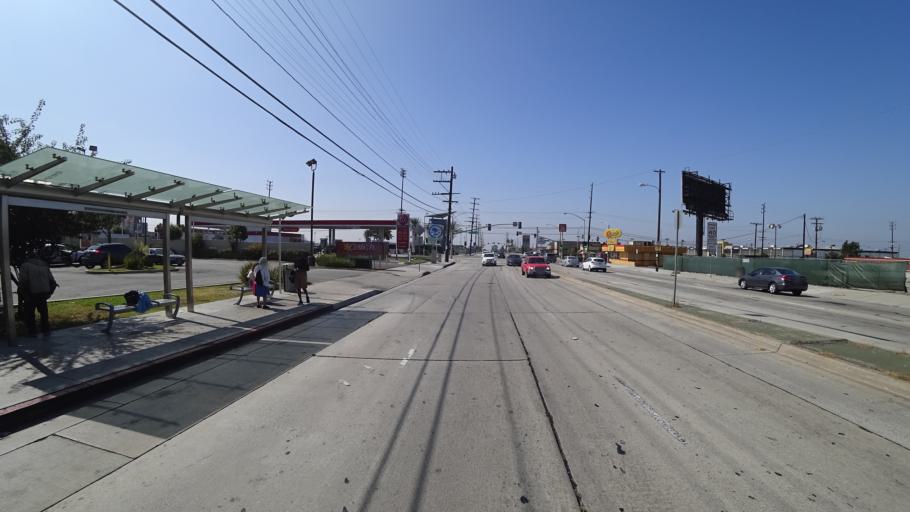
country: US
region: California
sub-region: Los Angeles County
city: West Athens
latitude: 33.9318
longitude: -118.3090
